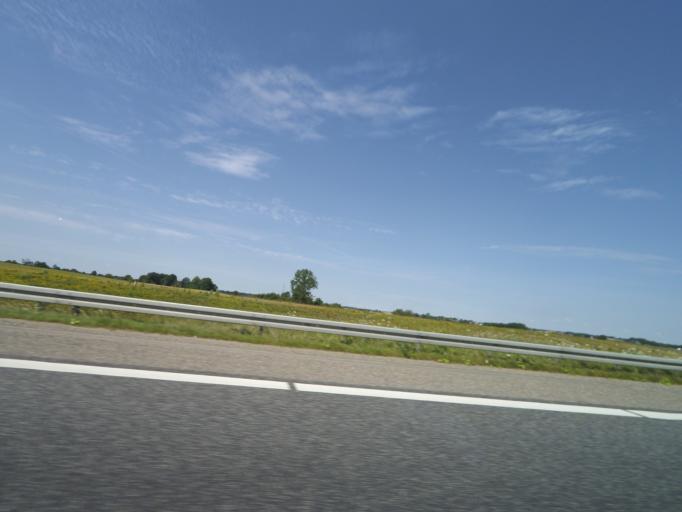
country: DK
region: South Denmark
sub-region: Vejle Kommune
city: Vejle
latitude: 55.7442
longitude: 9.5820
